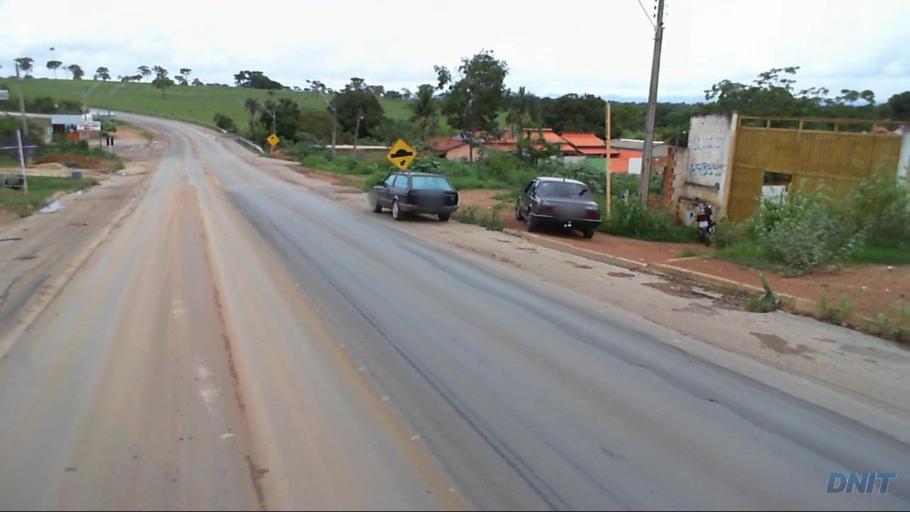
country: BR
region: Goias
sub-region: Padre Bernardo
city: Padre Bernardo
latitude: -15.1649
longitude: -48.2938
